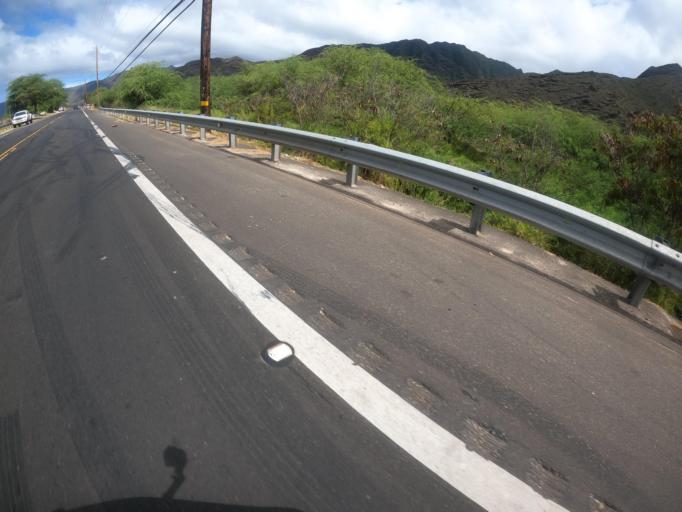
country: US
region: Hawaii
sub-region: Honolulu County
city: Makaha
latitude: 21.4970
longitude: -158.2291
